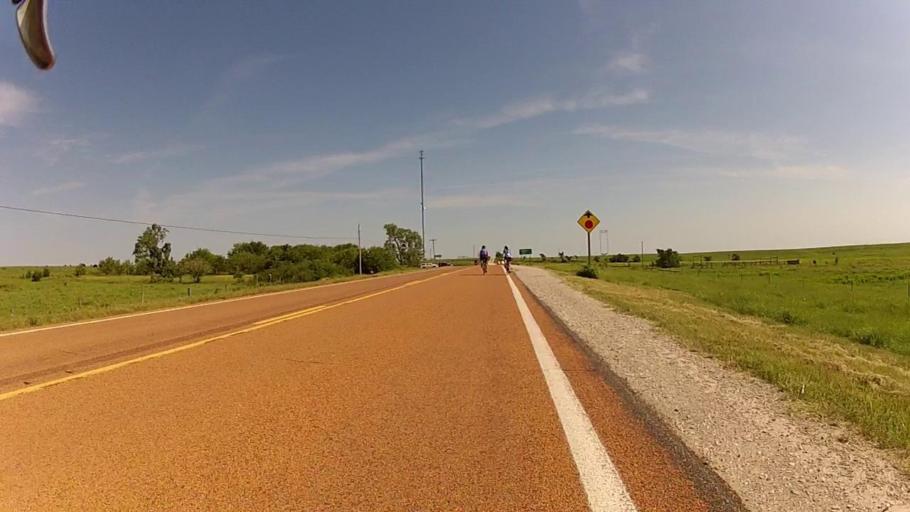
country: US
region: Kansas
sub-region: Cowley County
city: Winfield
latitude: 37.1088
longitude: -96.6436
